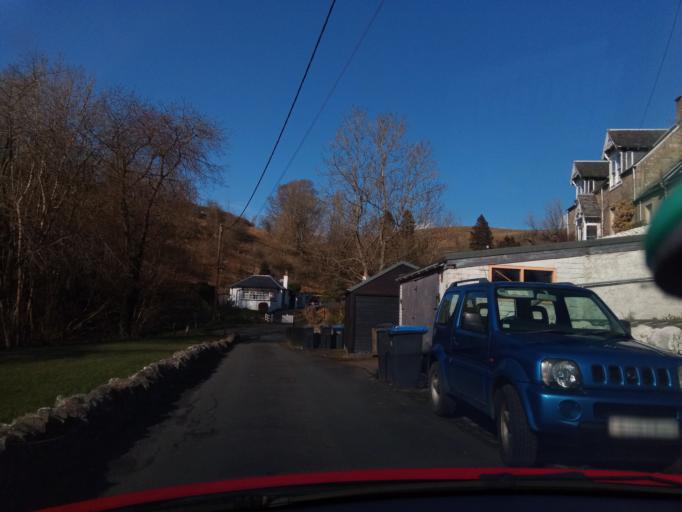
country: GB
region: Scotland
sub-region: The Scottish Borders
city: Hawick
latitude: 55.4235
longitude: -2.8072
